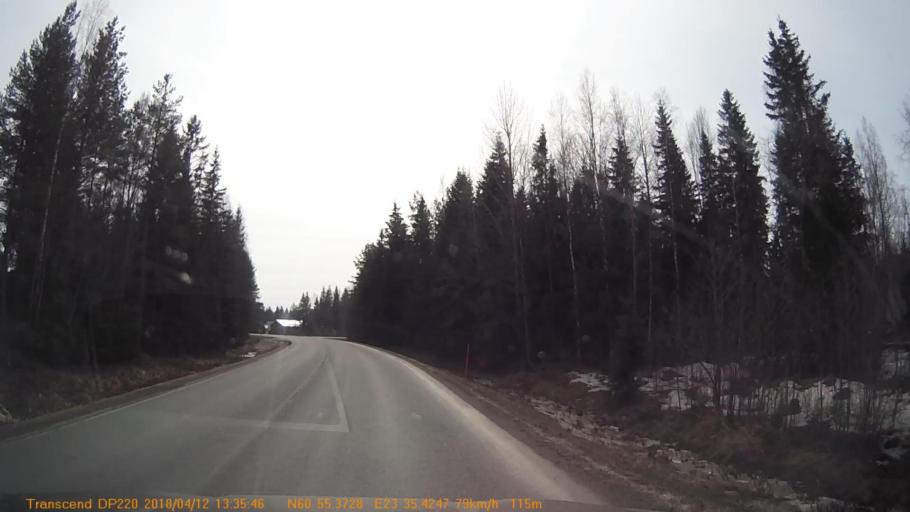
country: FI
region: Haeme
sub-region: Forssa
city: Forssa
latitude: 60.9225
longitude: 23.5901
